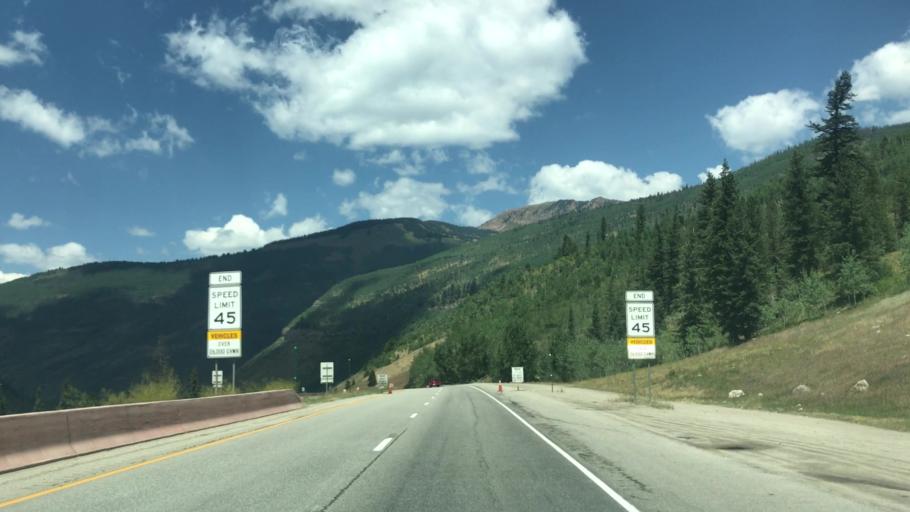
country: US
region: Colorado
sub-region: Eagle County
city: Vail
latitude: 39.6370
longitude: -106.2949
